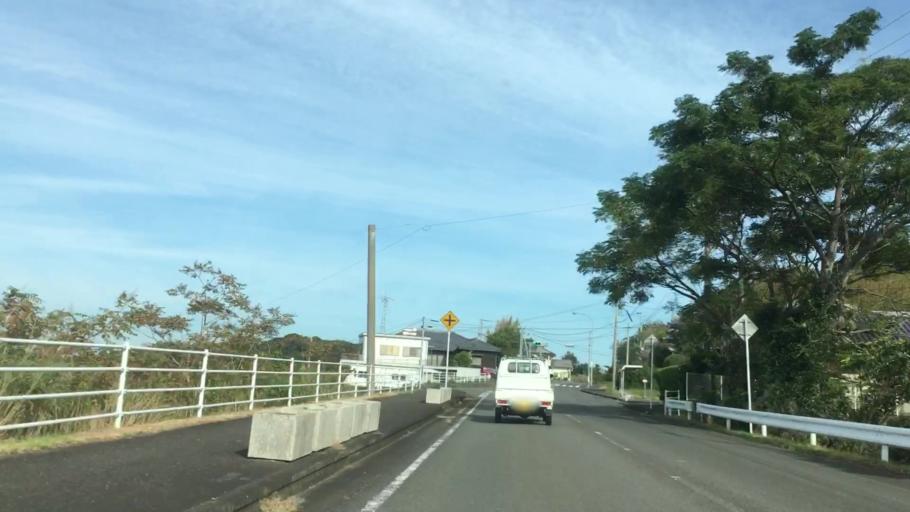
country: JP
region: Nagasaki
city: Sasebo
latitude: 33.0144
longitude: 129.6550
